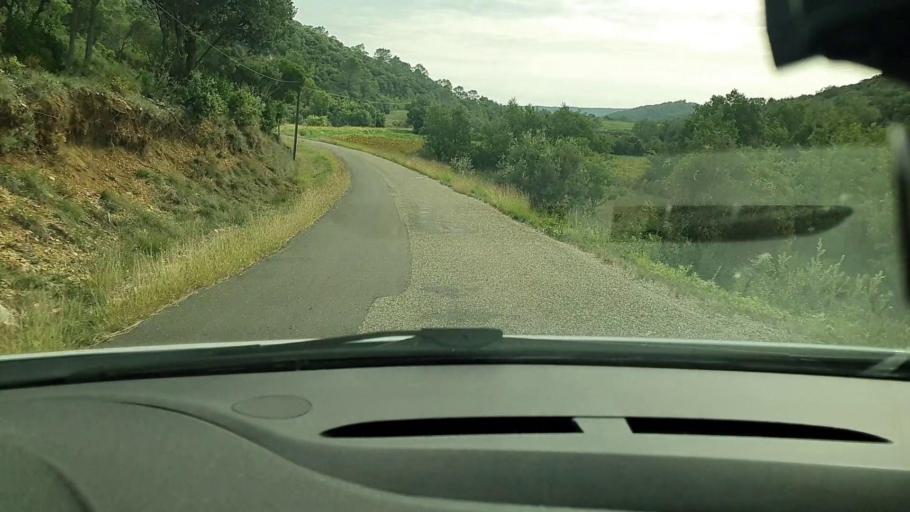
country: FR
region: Languedoc-Roussillon
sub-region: Departement du Gard
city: Montaren-et-Saint-Mediers
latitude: 44.0923
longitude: 4.3299
